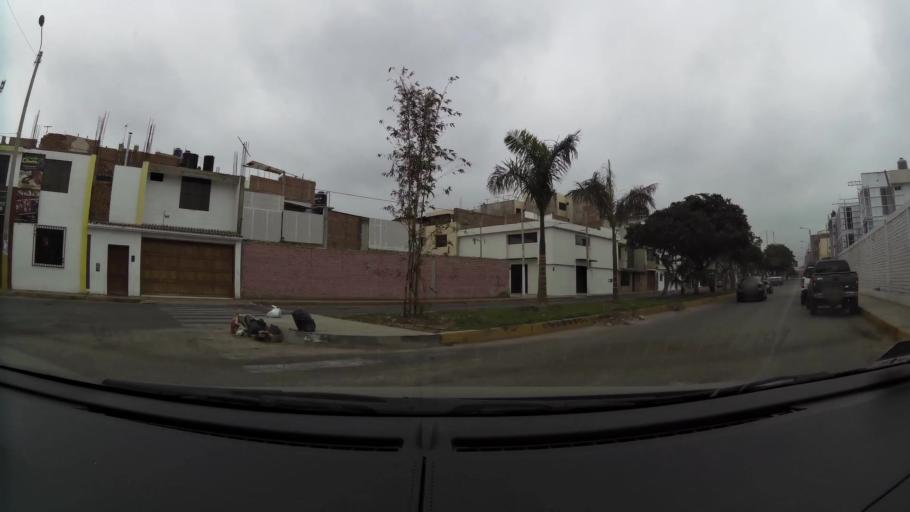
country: PE
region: La Libertad
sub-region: Provincia de Trujillo
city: Trujillo
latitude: -8.1207
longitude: -79.0292
